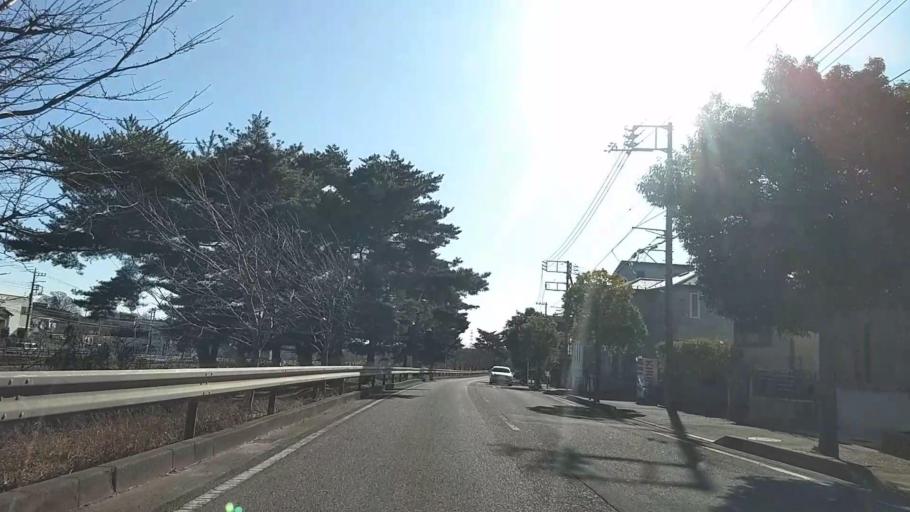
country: JP
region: Kanagawa
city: Hadano
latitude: 35.3905
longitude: 139.1849
